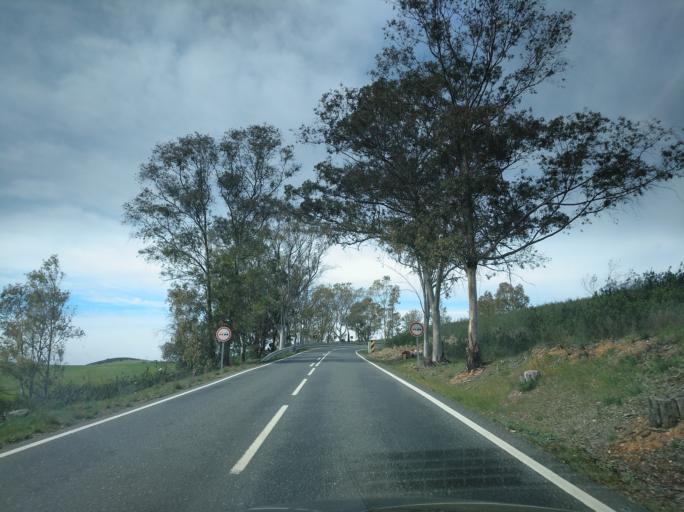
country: PT
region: Beja
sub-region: Mertola
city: Mertola
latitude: 37.7070
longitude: -7.7520
